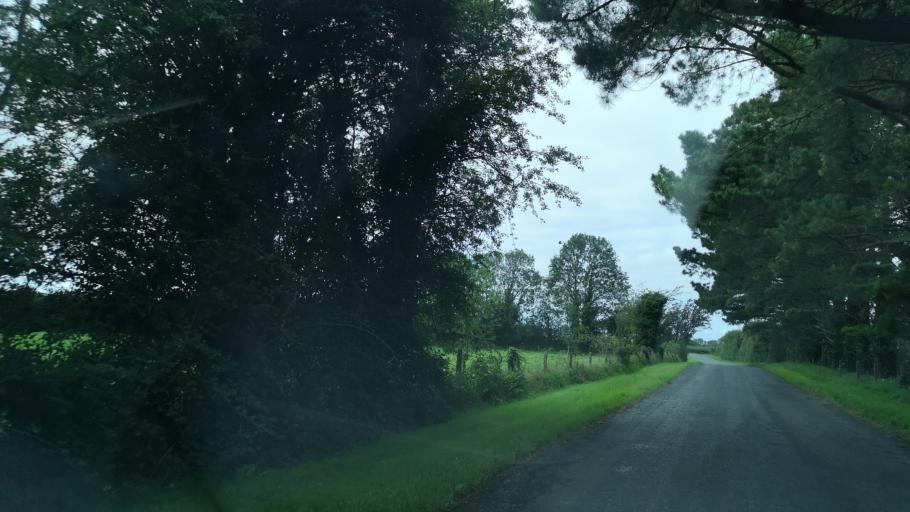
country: IE
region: Leinster
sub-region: Uibh Fhaili
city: Ferbane
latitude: 53.2305
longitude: -7.7294
